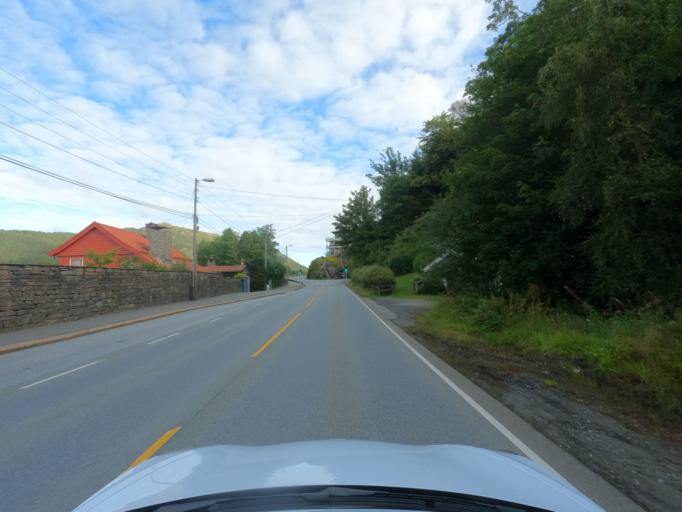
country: NO
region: Hordaland
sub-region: Bergen
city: Bergen
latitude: 60.3408
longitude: 5.3454
